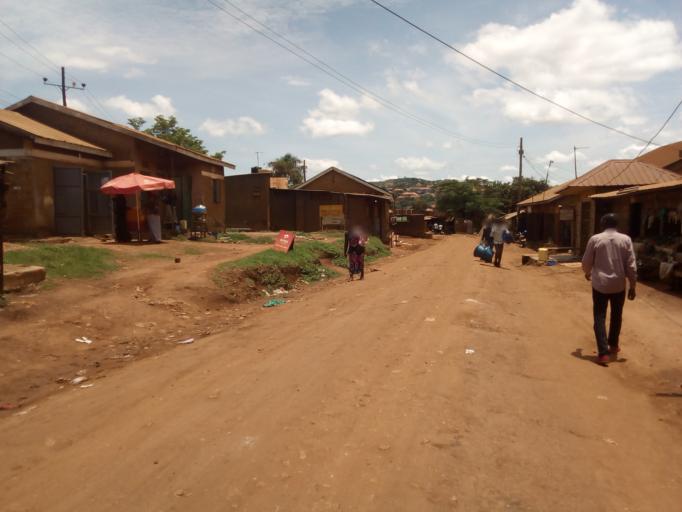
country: UG
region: Central Region
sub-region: Kampala District
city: Kampala
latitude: 0.2565
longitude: 32.5707
